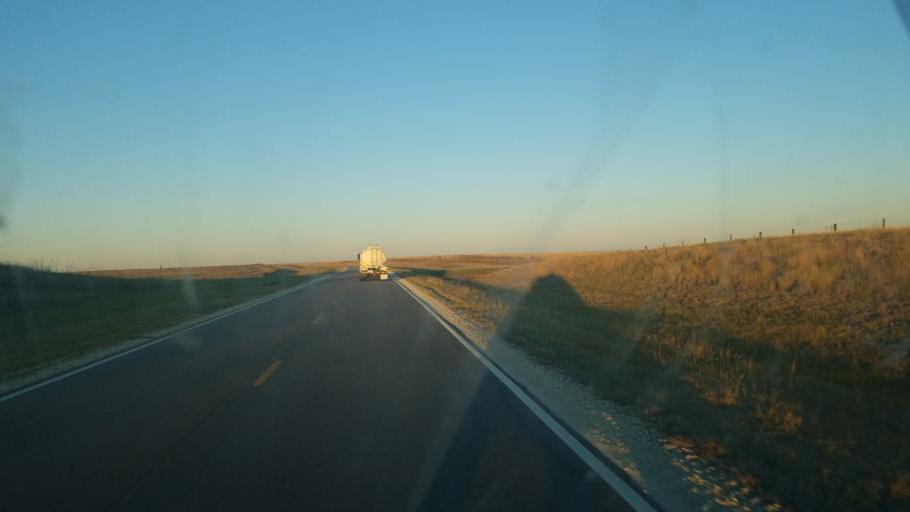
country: US
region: Kansas
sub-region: Wallace County
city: Sharon Springs
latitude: 38.8868
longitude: -101.8886
